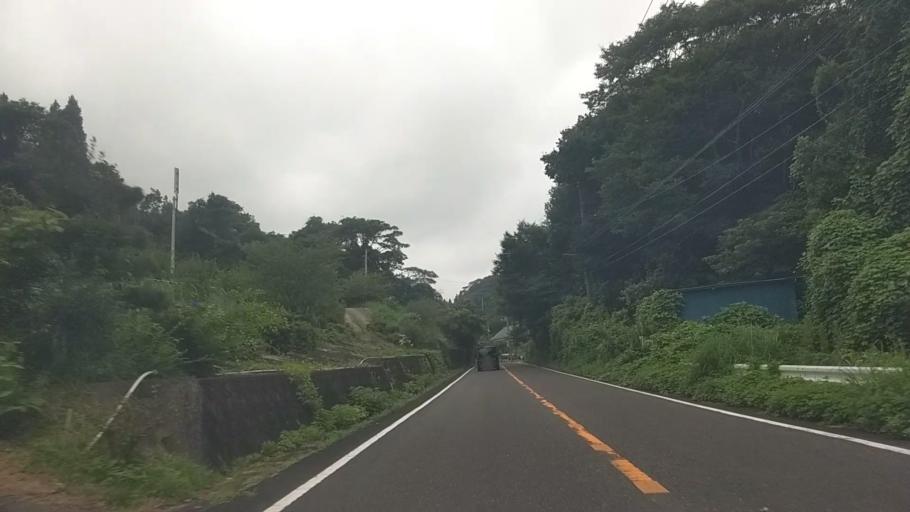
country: JP
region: Chiba
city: Kawaguchi
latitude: 35.1431
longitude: 139.9409
